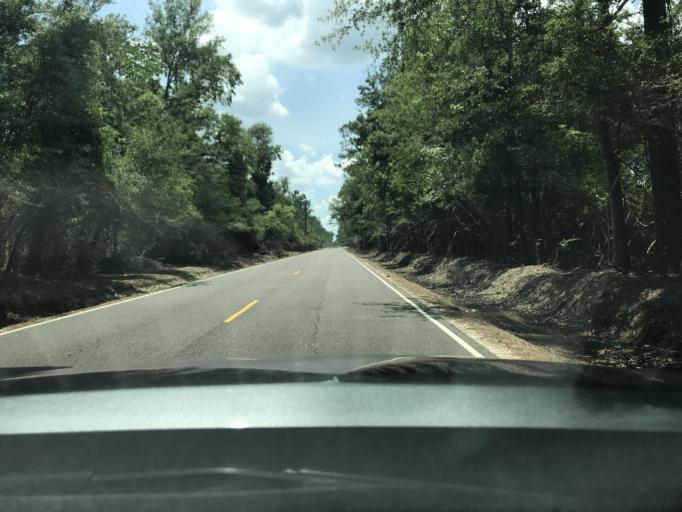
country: US
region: Louisiana
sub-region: Calcasieu Parish
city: Moss Bluff
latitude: 30.3298
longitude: -93.1375
